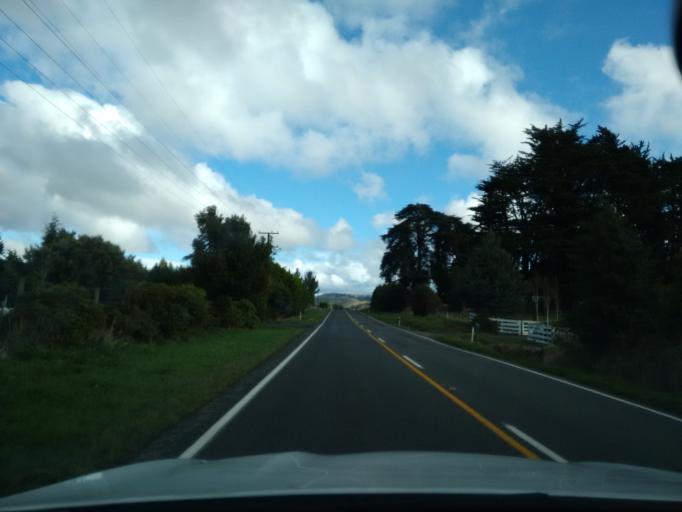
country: NZ
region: Manawatu-Wanganui
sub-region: Ruapehu District
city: Waiouru
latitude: -39.4090
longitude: 175.2847
